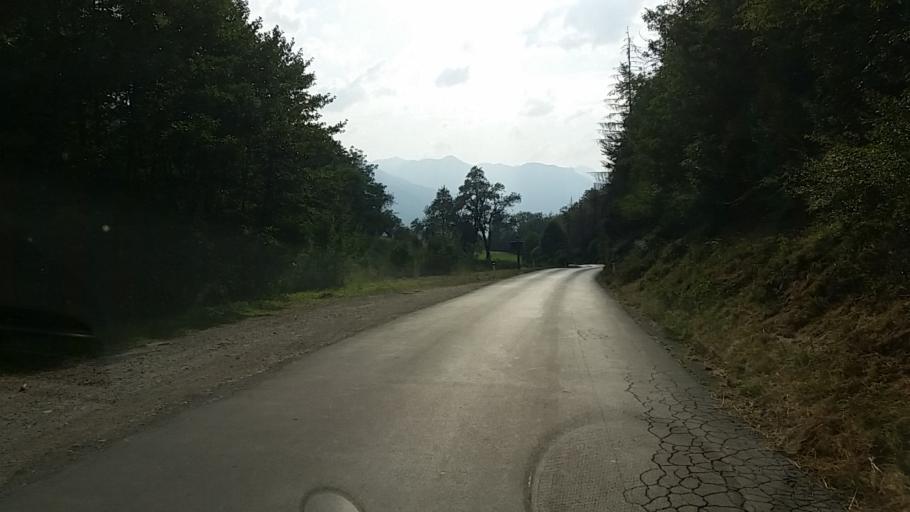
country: SI
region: Bohinj
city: Bohinjska Bistrica
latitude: 46.2727
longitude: 13.9809
